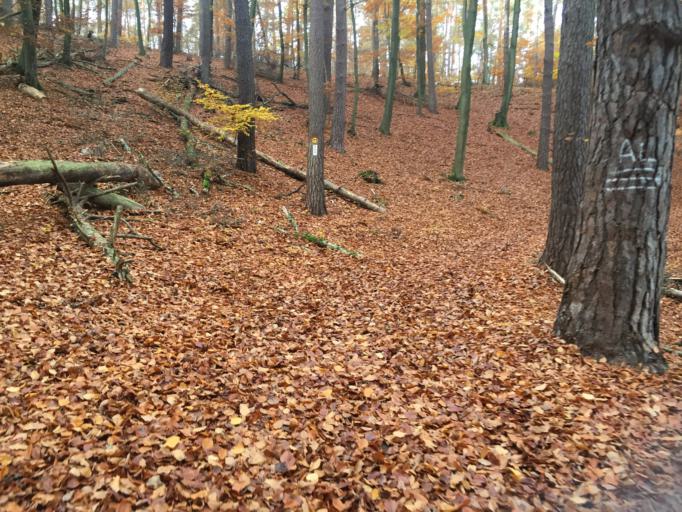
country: DE
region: Rheinland-Pfalz
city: Altleiningen
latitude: 49.4940
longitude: 8.0721
